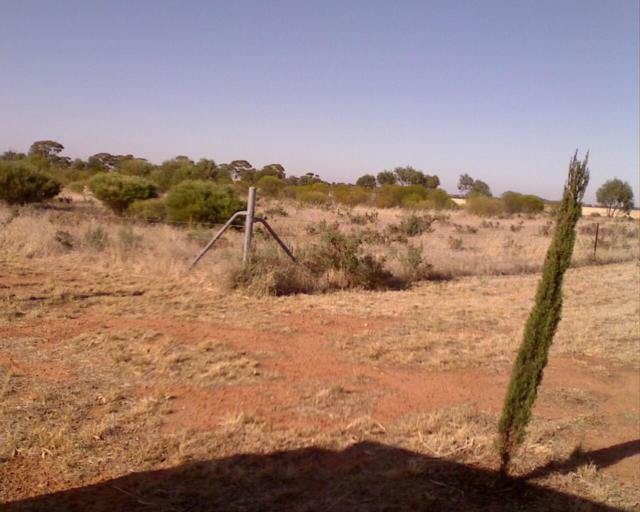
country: AU
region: Western Australia
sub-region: Merredin
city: Merredin
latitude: -31.1110
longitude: 117.7866
